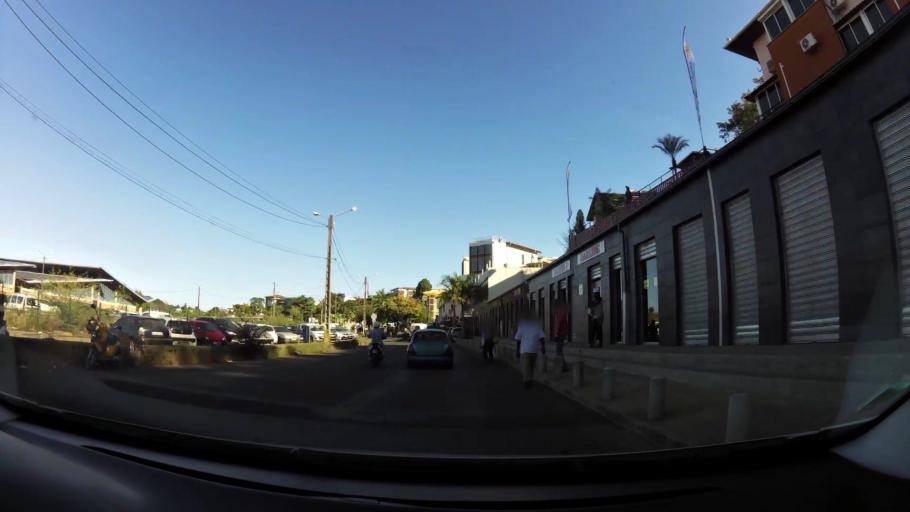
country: YT
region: Mamoudzou
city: Mamoudzou
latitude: -12.7766
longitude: 45.2320
